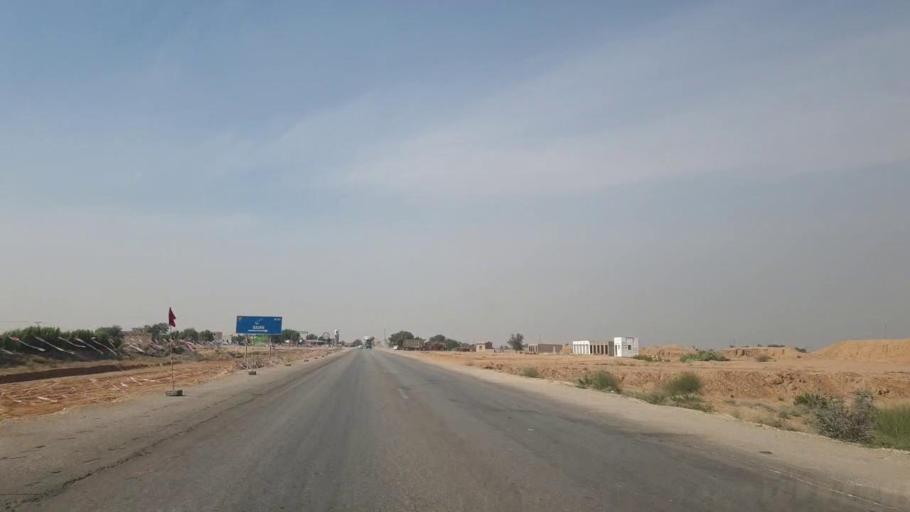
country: PK
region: Sindh
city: Sann
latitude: 26.0259
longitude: 68.1282
